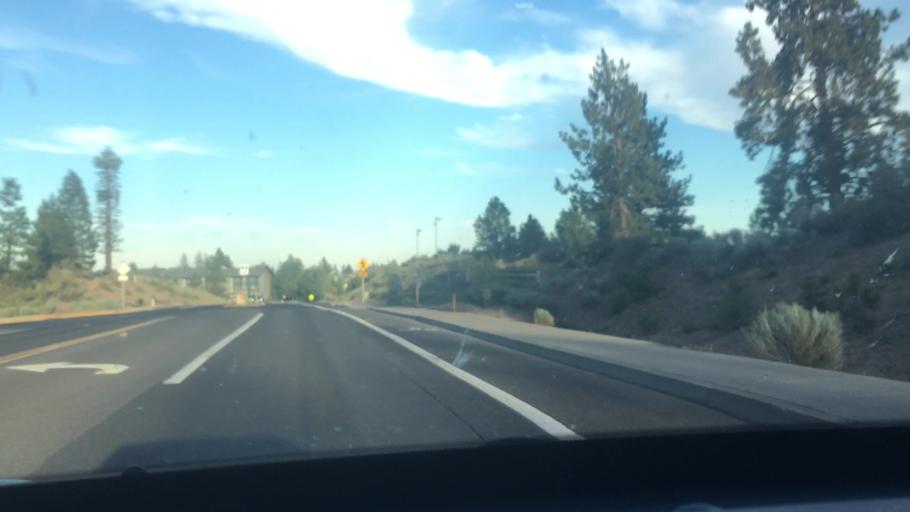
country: US
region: Oregon
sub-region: Deschutes County
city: Bend
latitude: 44.0407
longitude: -121.3413
